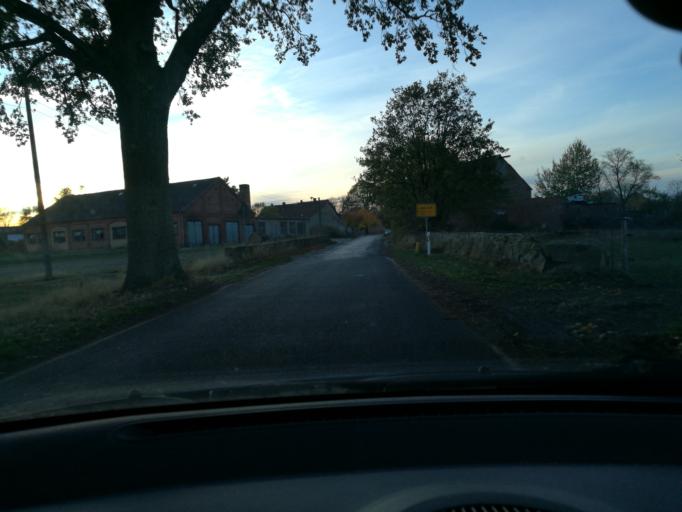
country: DE
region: Brandenburg
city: Karstadt
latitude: 53.0991
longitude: 11.7002
